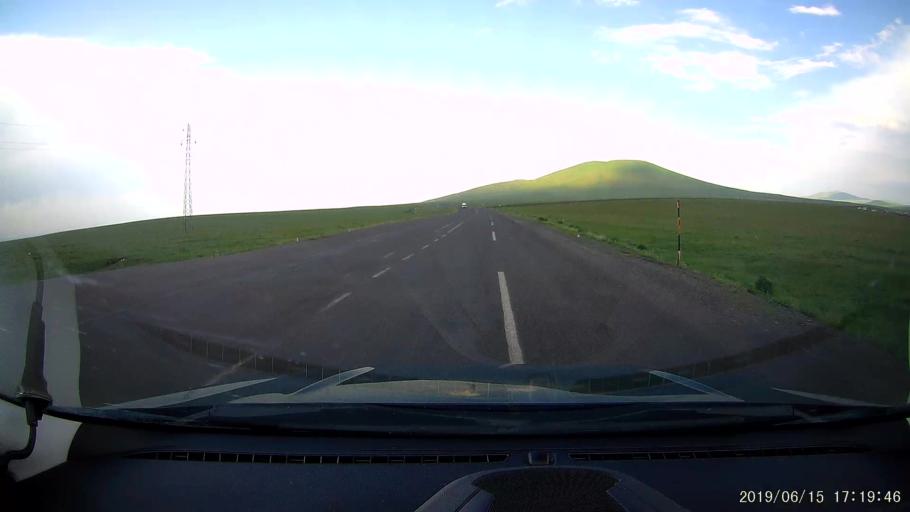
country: TR
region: Kars
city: Kars
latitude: 40.6161
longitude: 43.2859
